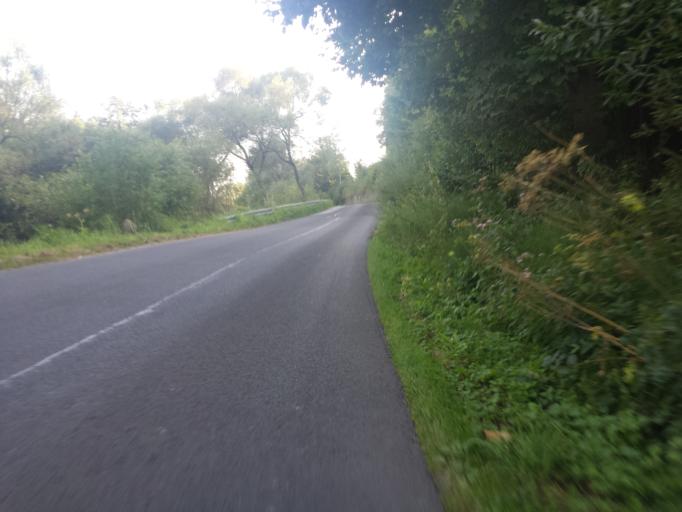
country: PL
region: Subcarpathian Voivodeship
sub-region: Powiat leski
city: Uherce Mineralne
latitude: 49.4611
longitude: 22.3966
